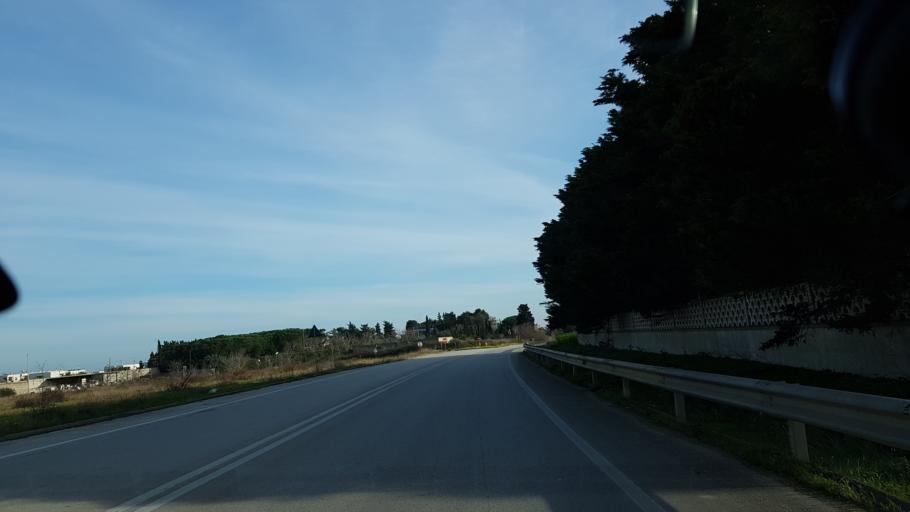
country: IT
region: Apulia
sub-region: Provincia di Brindisi
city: Brindisi
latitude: 40.6439
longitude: 17.9120
